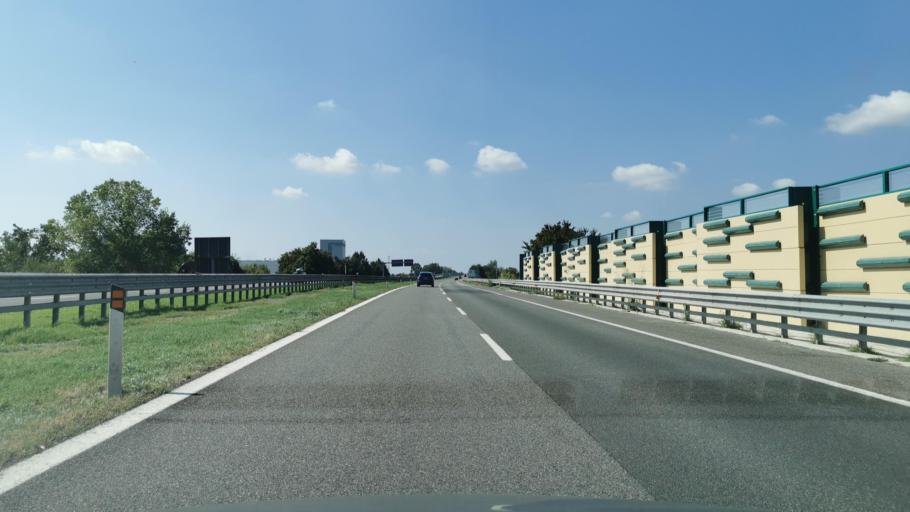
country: IT
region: Emilia-Romagna
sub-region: Provincia di Piacenza
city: Castelvetro Piacentino
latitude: 45.0863
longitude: 9.9933
